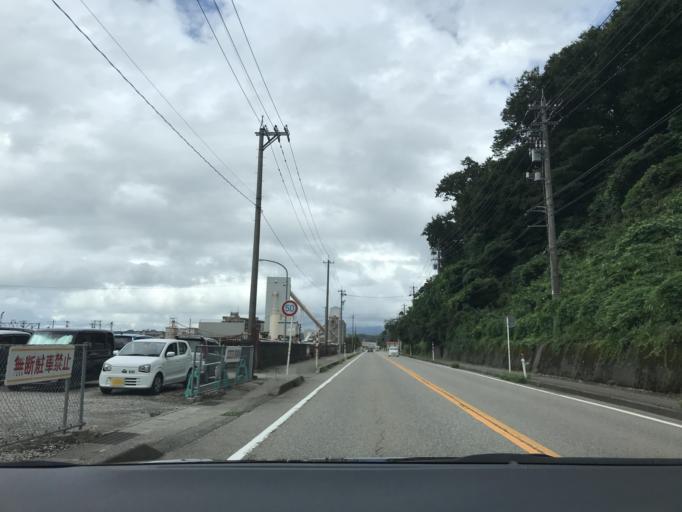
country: JP
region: Ishikawa
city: Tsubata
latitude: 36.6553
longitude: 136.7299
